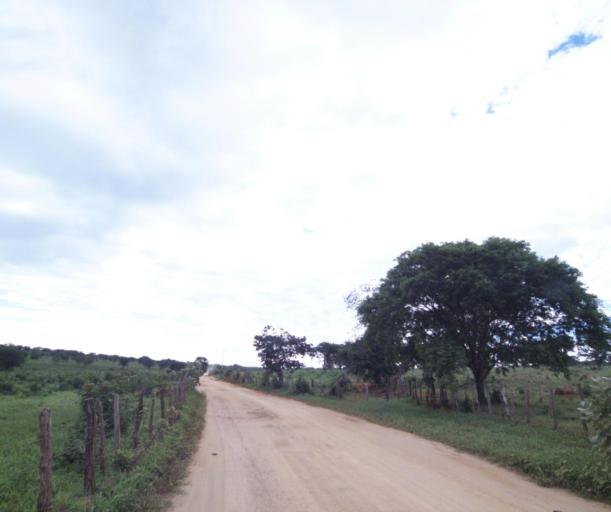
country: BR
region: Bahia
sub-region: Carinhanha
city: Carinhanha
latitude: -14.1810
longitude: -44.5103
